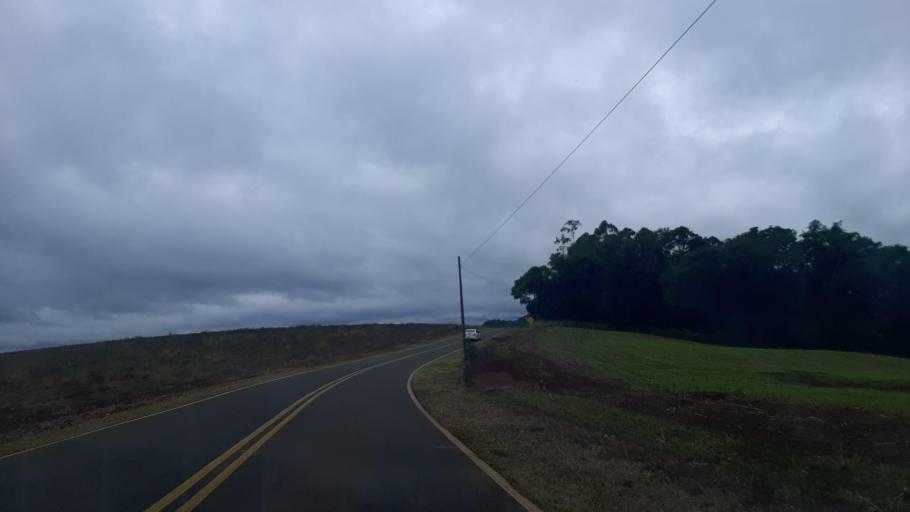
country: BR
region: Parana
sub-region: Ampere
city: Ampere
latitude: -25.9546
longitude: -53.4527
